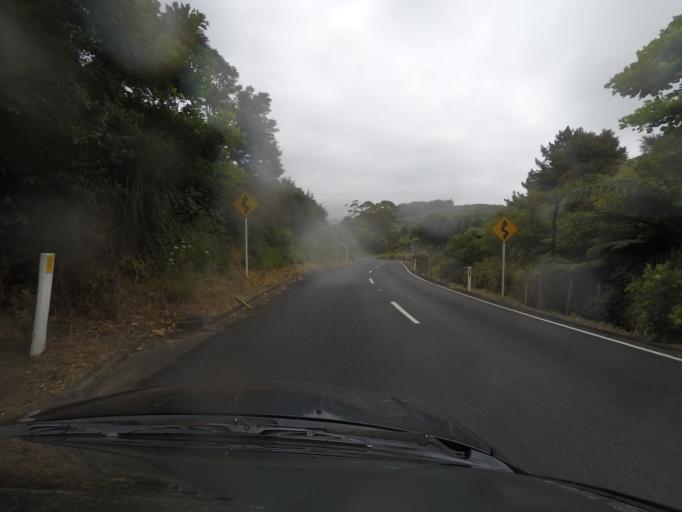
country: NZ
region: Auckland
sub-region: Auckland
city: Warkworth
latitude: -36.2795
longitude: 174.6939
